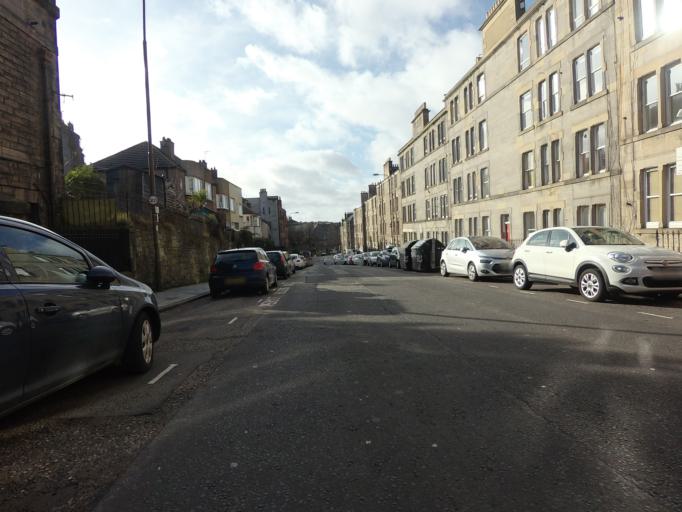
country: GB
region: Scotland
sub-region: Edinburgh
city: Edinburgh
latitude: 55.9652
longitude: -3.1903
